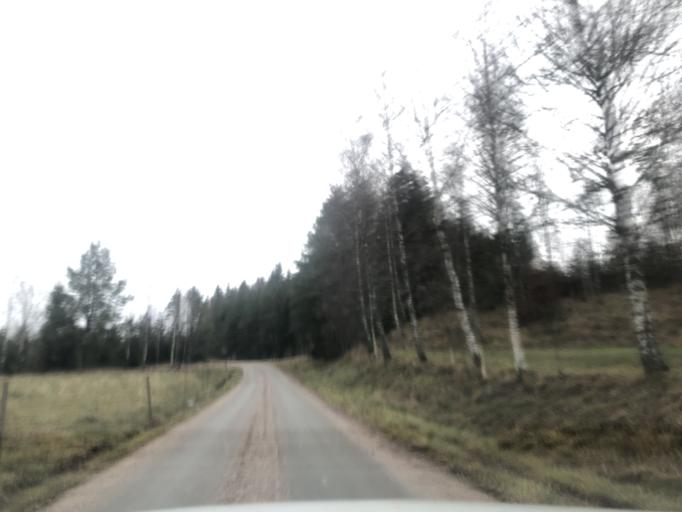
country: SE
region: Vaestra Goetaland
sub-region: Ulricehamns Kommun
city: Ulricehamn
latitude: 57.8920
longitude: 13.4707
